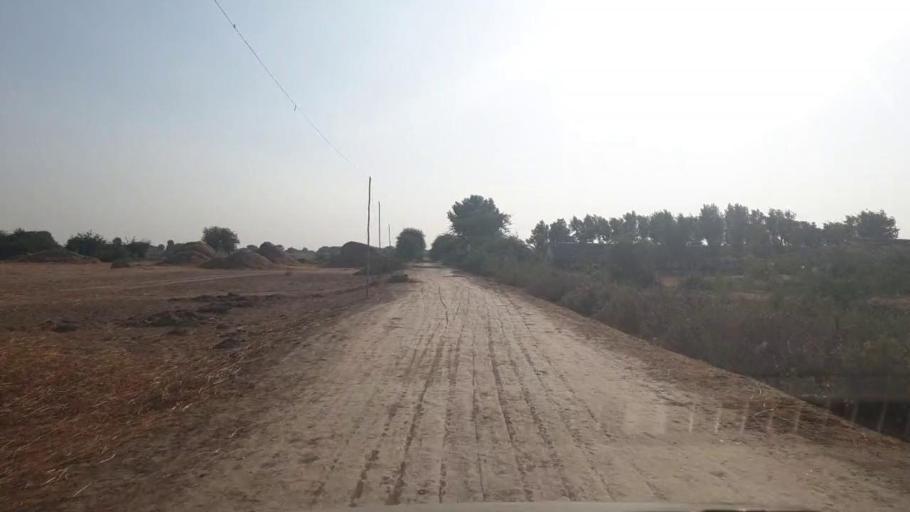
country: PK
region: Sindh
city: Badin
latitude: 24.6420
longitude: 68.8020
